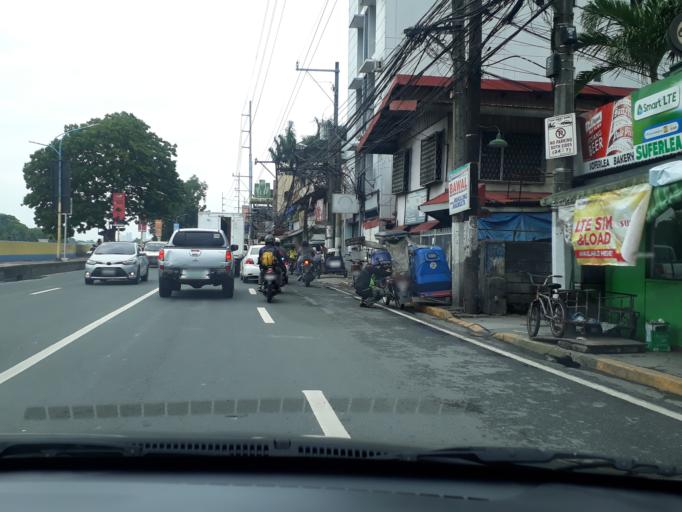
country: PH
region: Metro Manila
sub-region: Mandaluyong
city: Mandaluyong City
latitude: 14.5715
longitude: 121.0303
